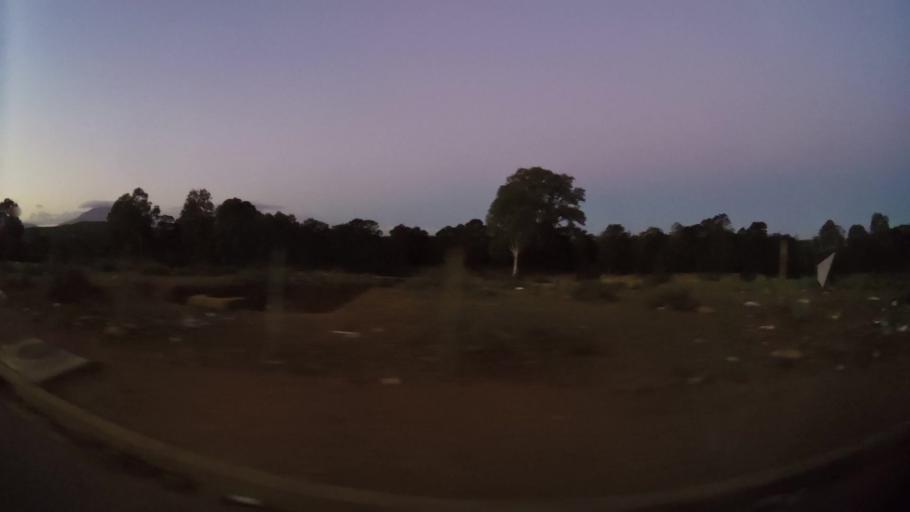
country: ZA
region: Western Cape
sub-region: Eden District Municipality
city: Riversdale
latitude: -34.1047
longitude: 21.2745
